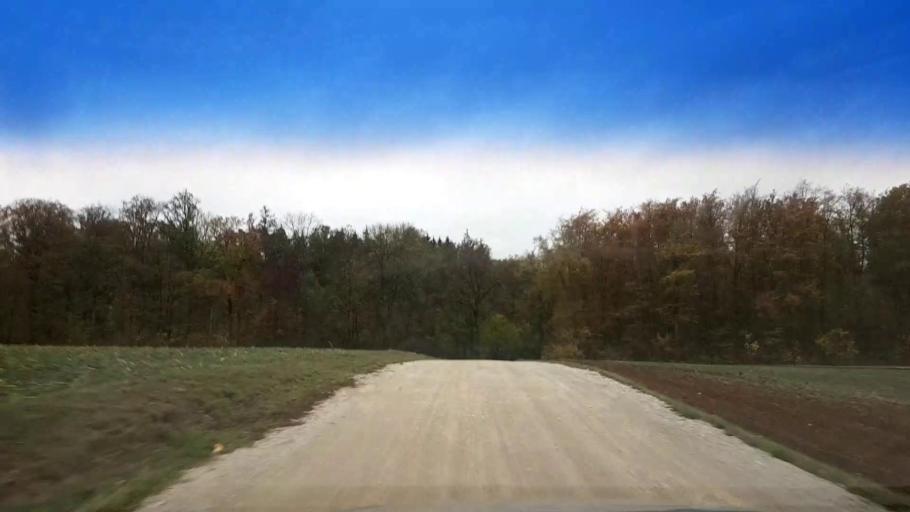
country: DE
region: Bavaria
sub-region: Upper Franconia
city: Schesslitz
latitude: 49.9654
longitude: 11.0320
